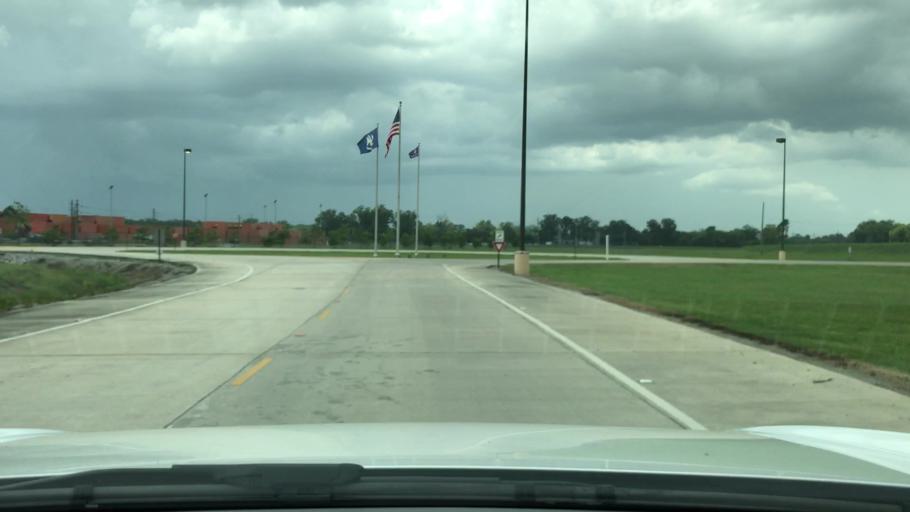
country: US
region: Louisiana
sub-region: Iberville Parish
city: Saint Gabriel
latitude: 30.2700
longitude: -91.1462
